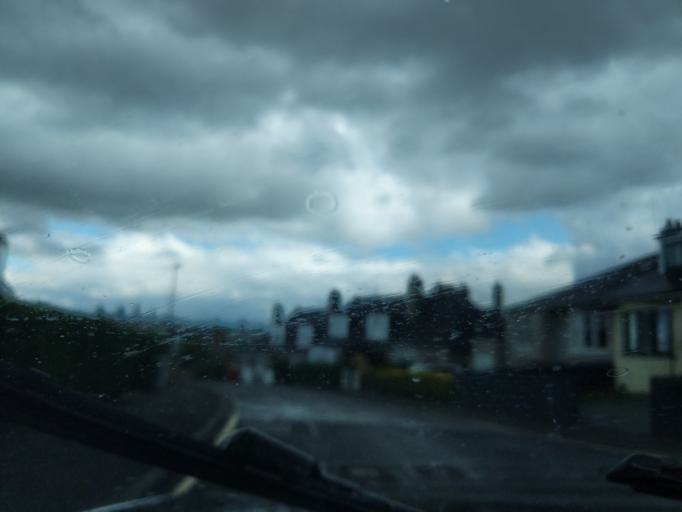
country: GB
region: Scotland
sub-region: Edinburgh
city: Edinburgh
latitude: 55.9582
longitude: -3.2376
